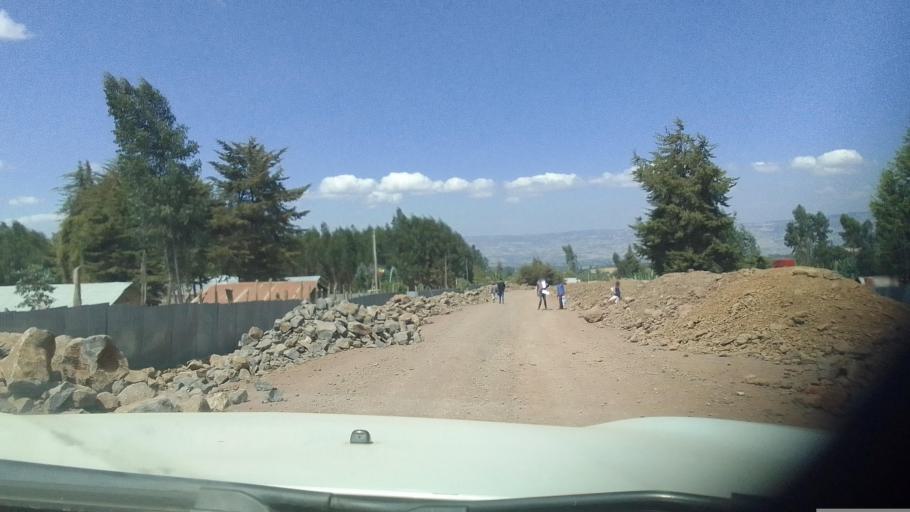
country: ET
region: Oromiya
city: Hagere Hiywet
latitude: 8.8604
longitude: 37.8907
